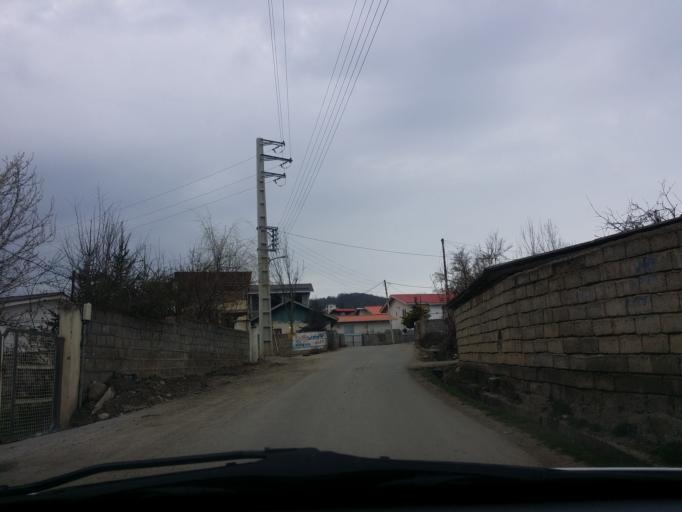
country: IR
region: Mazandaran
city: `Abbasabad
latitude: 36.5483
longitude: 51.1654
